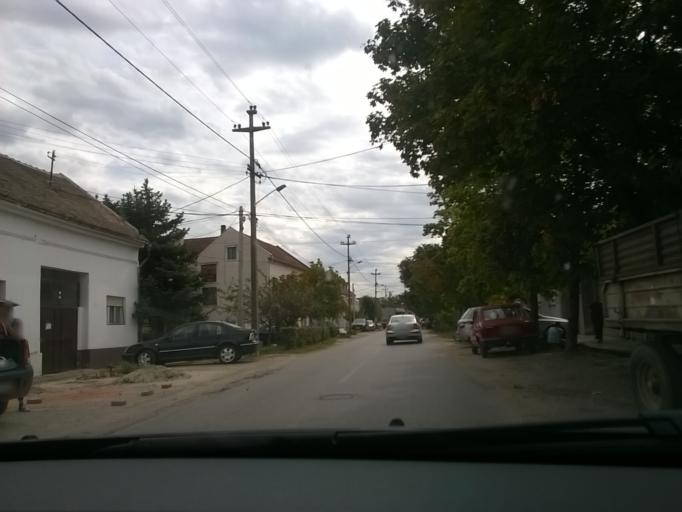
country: RS
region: Autonomna Pokrajina Vojvodina
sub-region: Juznobanatski Okrug
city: Vrsac
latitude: 45.1244
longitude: 21.3003
